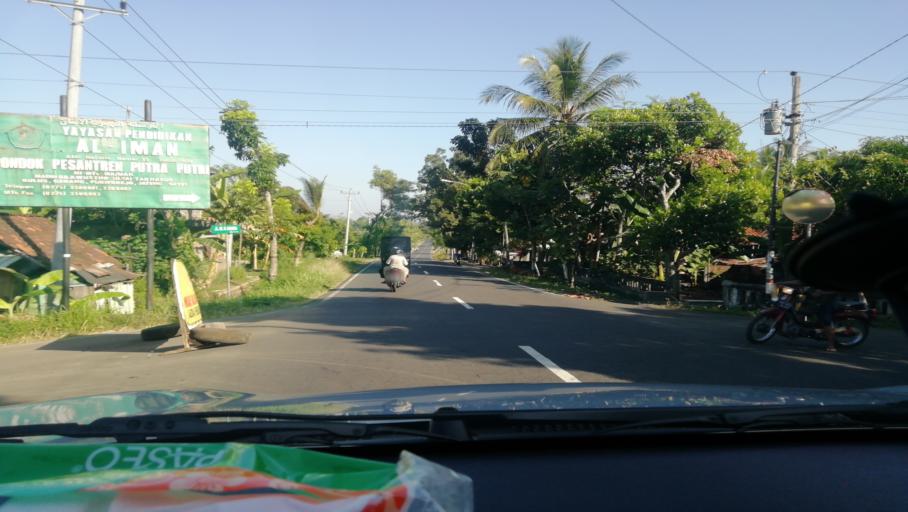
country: ID
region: Central Java
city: Kutoarjo
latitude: -7.6993
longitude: 110.0078
